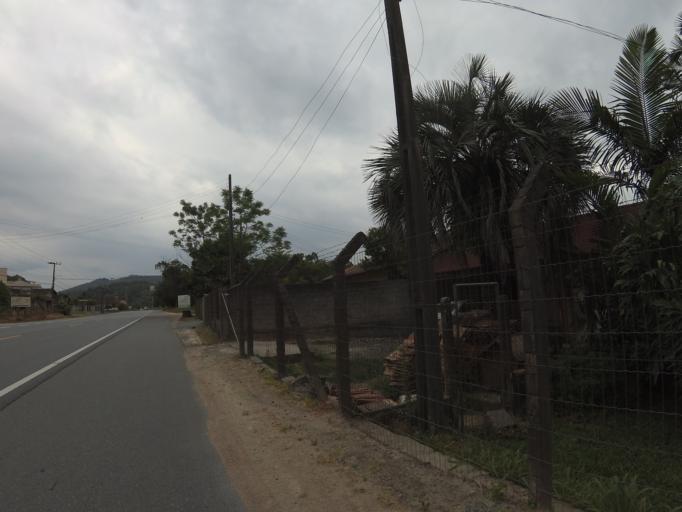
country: BR
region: Santa Catarina
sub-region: Pomerode
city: Pomerode
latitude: -26.8303
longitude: -49.1619
